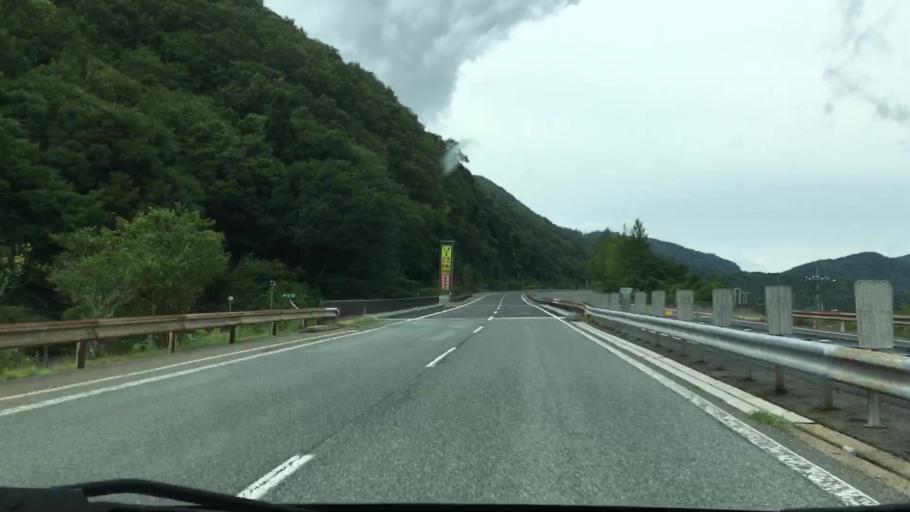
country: JP
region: Okayama
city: Niimi
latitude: 34.9715
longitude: 133.6250
